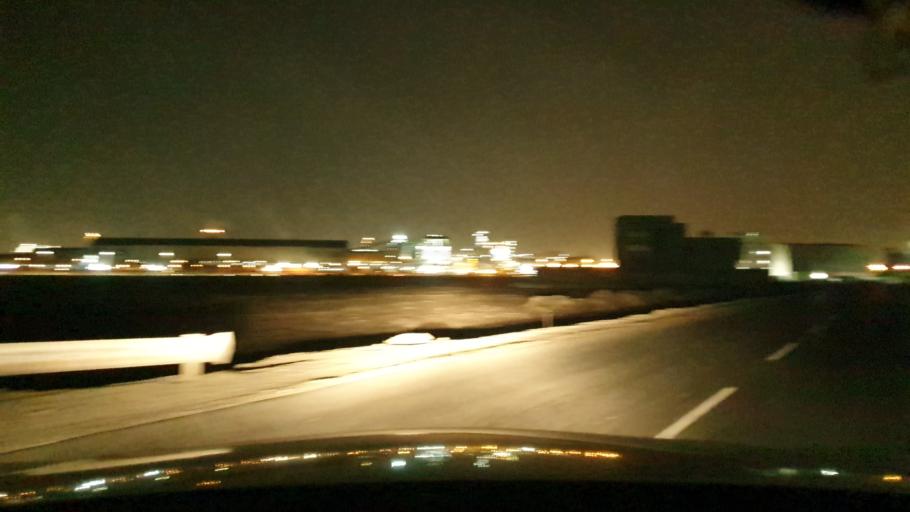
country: BH
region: Northern
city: Sitrah
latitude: 26.0939
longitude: 50.6147
